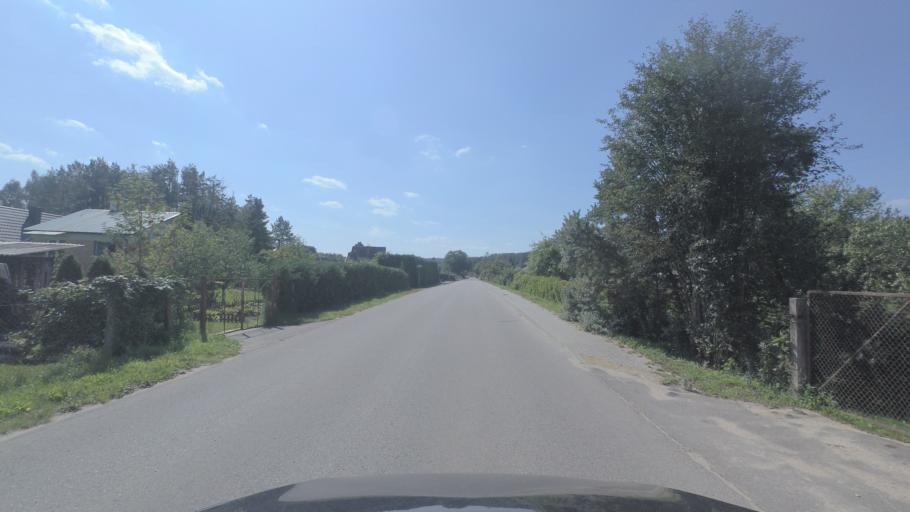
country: LT
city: Nemencine
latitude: 54.8575
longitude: 25.3846
